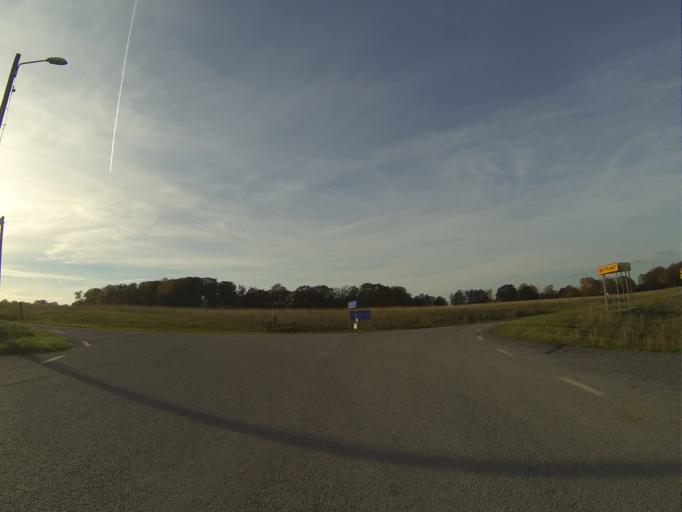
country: SE
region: Skane
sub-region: Lunds Kommun
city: Veberod
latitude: 55.6977
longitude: 13.4237
